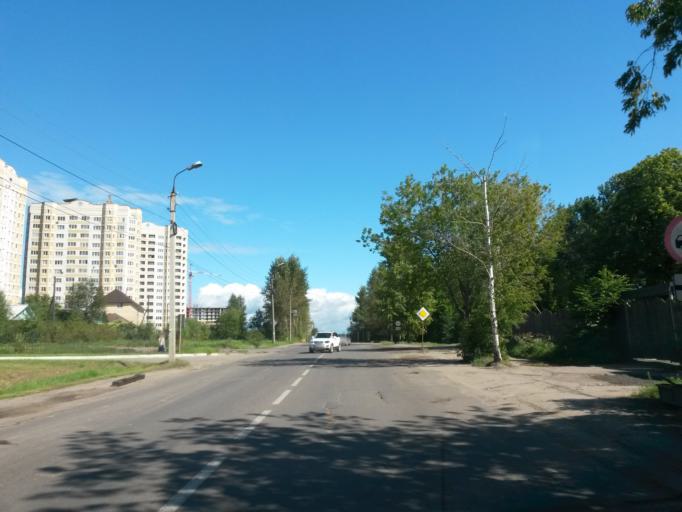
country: RU
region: Jaroslavl
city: Yaroslavl
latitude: 57.5766
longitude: 39.8674
